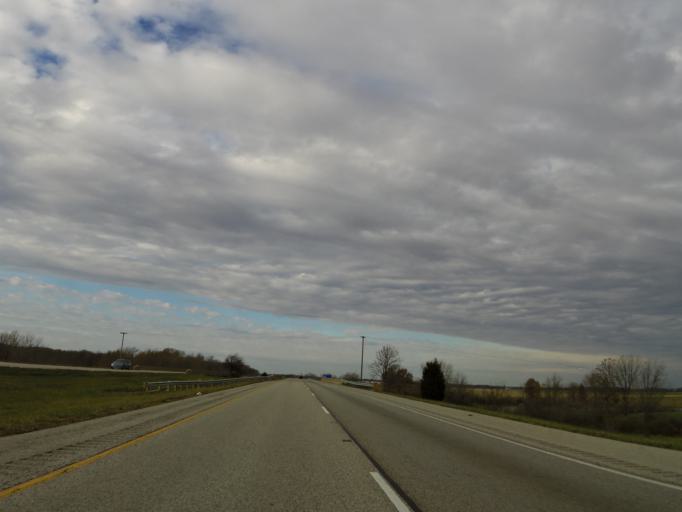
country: US
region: Illinois
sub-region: Washington County
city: Nashville
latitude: 38.3901
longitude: -89.3342
